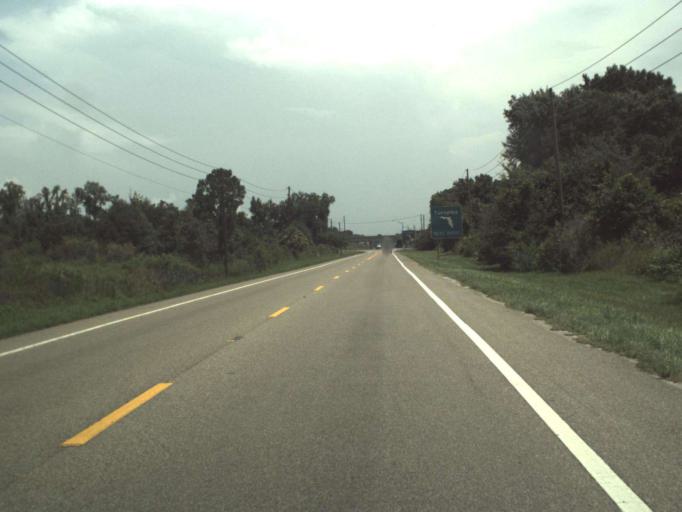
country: US
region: Florida
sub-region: Sumter County
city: Wildwood
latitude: 28.8324
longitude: -82.0455
